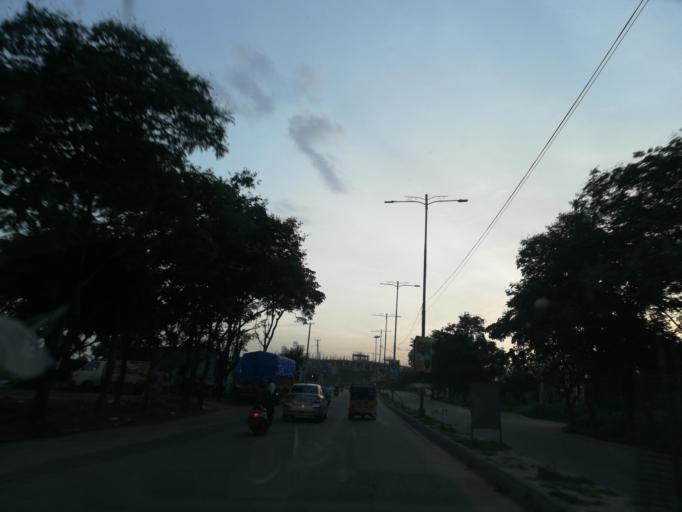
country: IN
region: Telangana
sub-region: Medak
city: Serilingampalle
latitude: 17.5397
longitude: 78.3606
